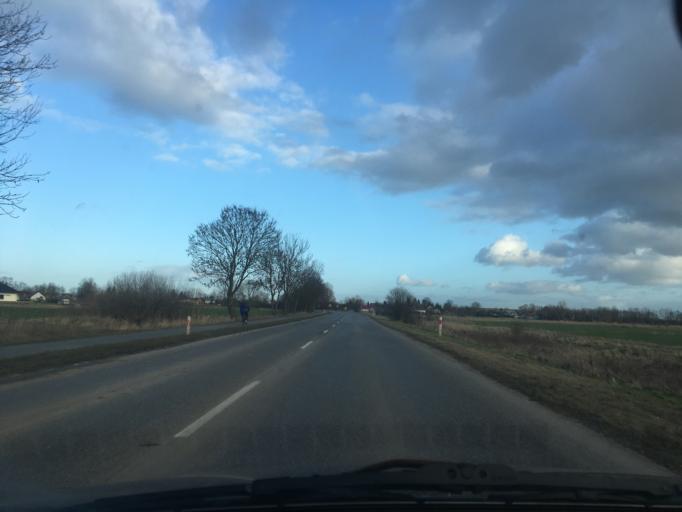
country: PL
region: Pomeranian Voivodeship
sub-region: Powiat gdanski
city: Cedry Wielkie
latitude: 54.3297
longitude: 18.7919
